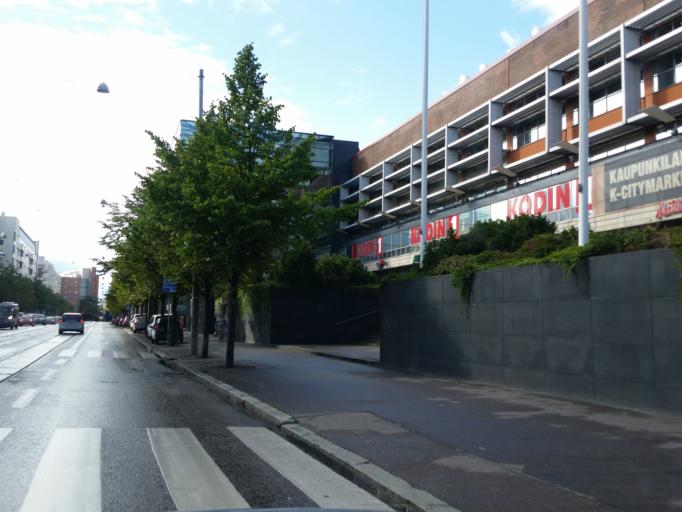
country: FI
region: Uusimaa
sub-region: Helsinki
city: Helsinki
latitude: 60.1633
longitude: 24.9127
